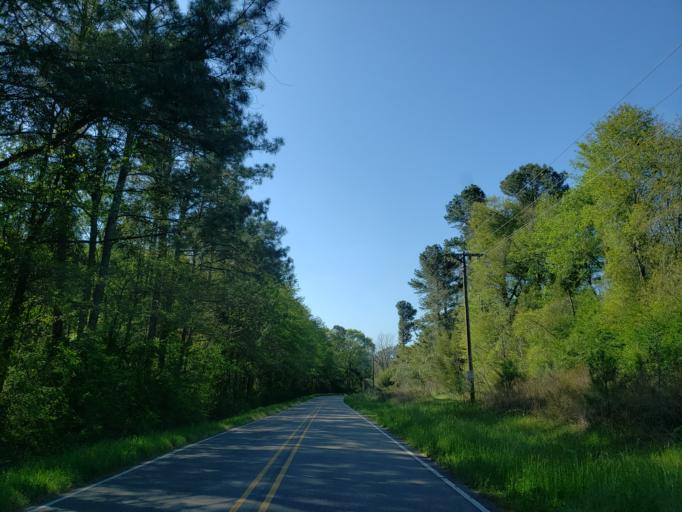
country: US
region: Mississippi
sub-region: Jones County
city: Ellisville
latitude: 31.5813
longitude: -89.3767
